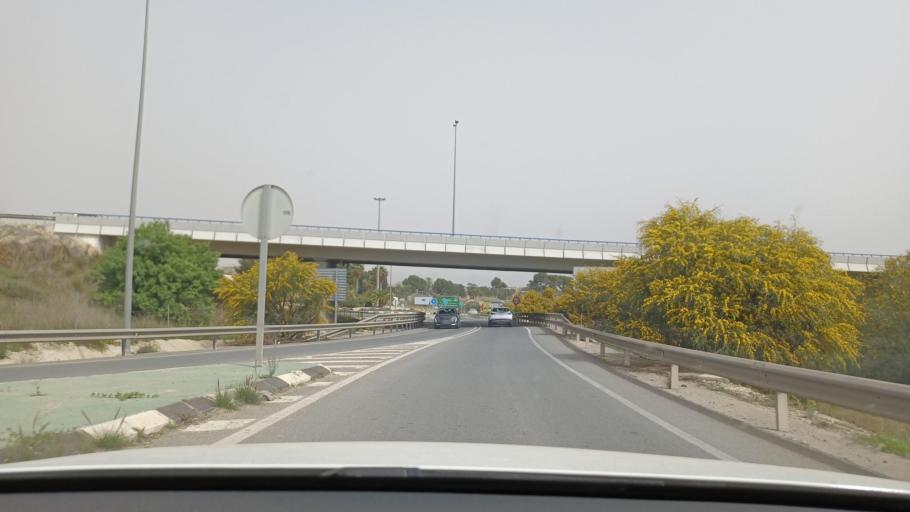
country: ES
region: Valencia
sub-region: Provincia de Alicante
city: San Vicent del Raspeig
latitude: 38.3837
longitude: -0.4887
